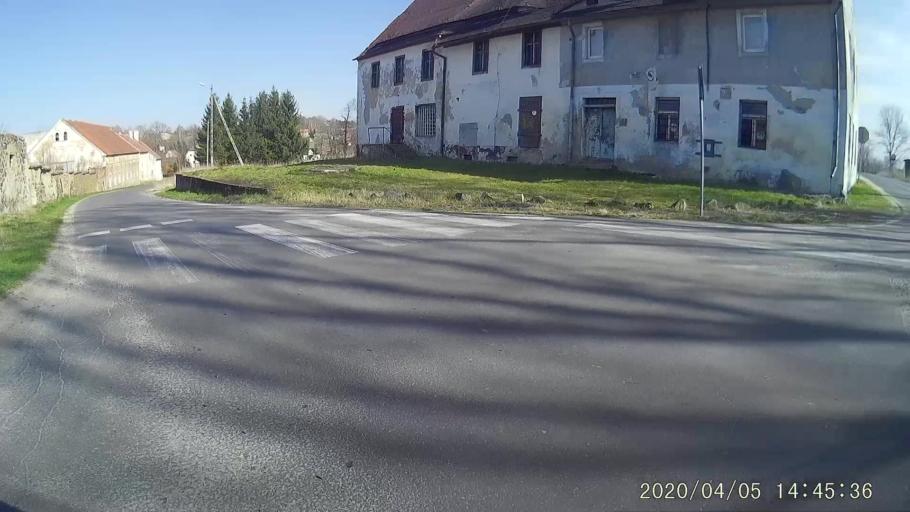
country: PL
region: Lower Silesian Voivodeship
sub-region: Powiat zgorzelecki
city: Sulikow
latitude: 51.0526
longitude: 15.1089
